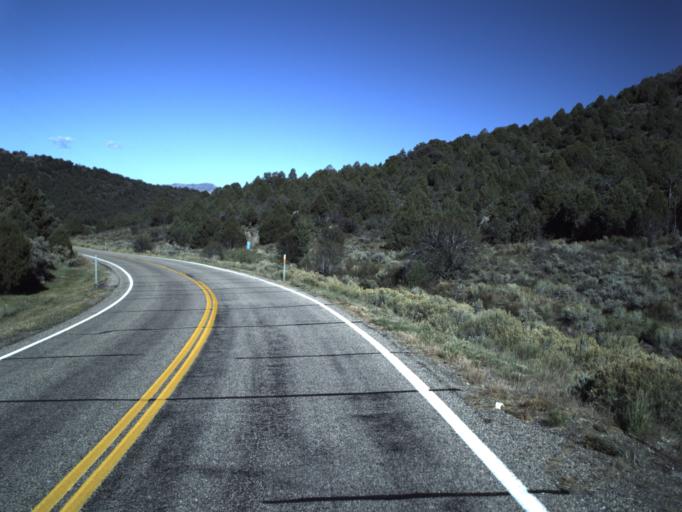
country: US
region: Utah
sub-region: Garfield County
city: Panguitch
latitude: 37.7607
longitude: -112.5059
